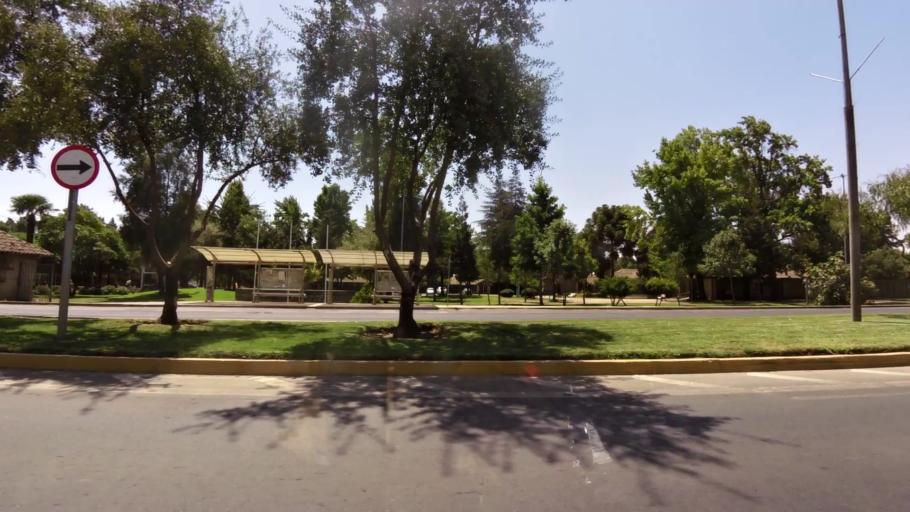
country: CL
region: Maule
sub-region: Provincia de Talca
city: Talca
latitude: -35.4367
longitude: -71.6224
